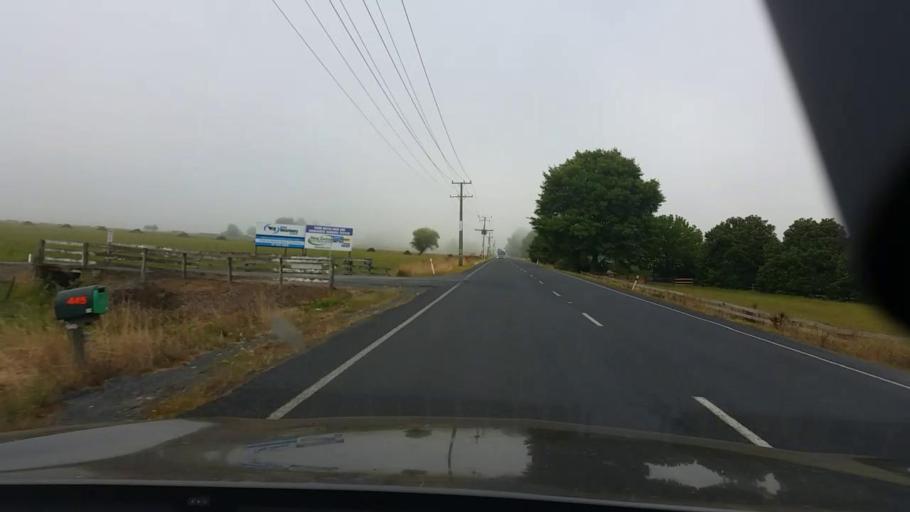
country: NZ
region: Waikato
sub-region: Hamilton City
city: Hamilton
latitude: -37.6279
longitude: 175.3182
